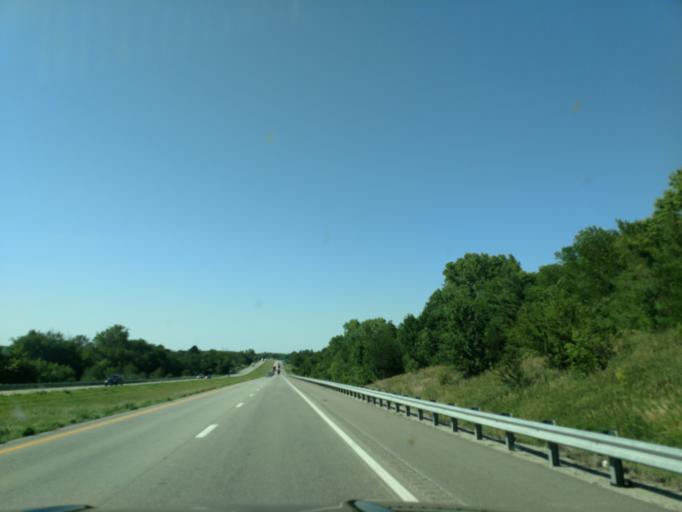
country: US
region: Missouri
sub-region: Andrew County
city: Country Club Village
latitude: 39.8346
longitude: -94.8052
